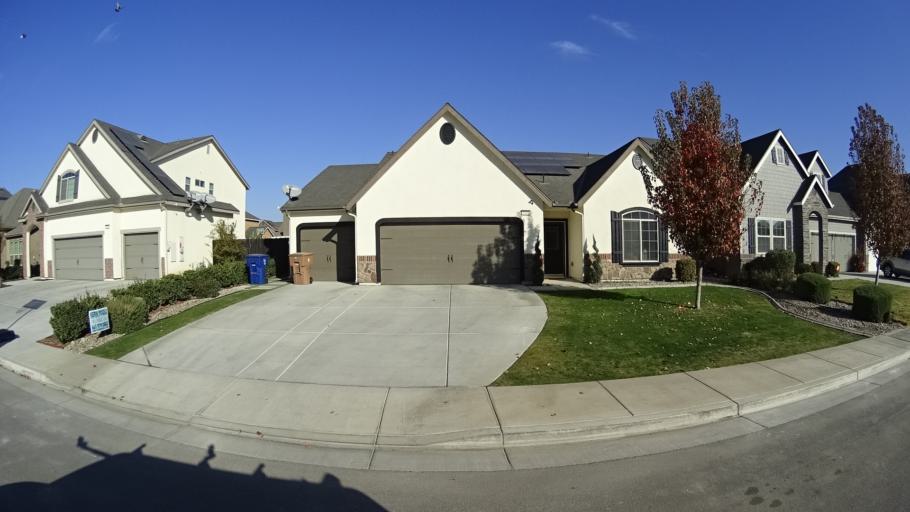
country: US
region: California
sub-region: Kern County
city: Greenfield
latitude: 35.2697
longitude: -119.0698
